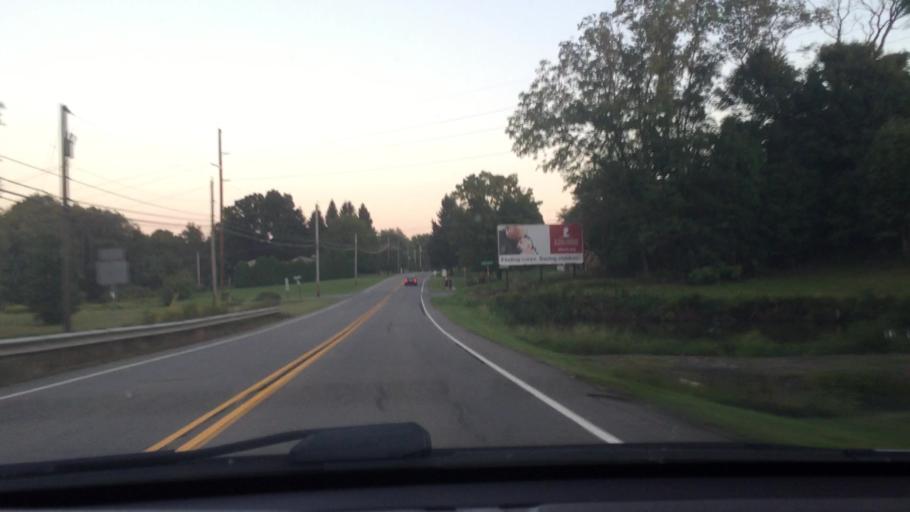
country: US
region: Pennsylvania
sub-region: Mercer County
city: Grove City
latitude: 41.1199
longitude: -80.0615
